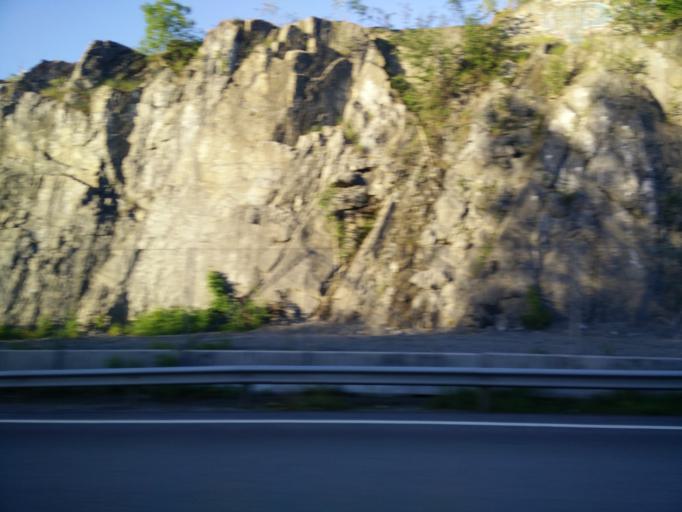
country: NO
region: Akershus
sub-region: Asker
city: Billingstad
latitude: 59.9023
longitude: 10.4945
